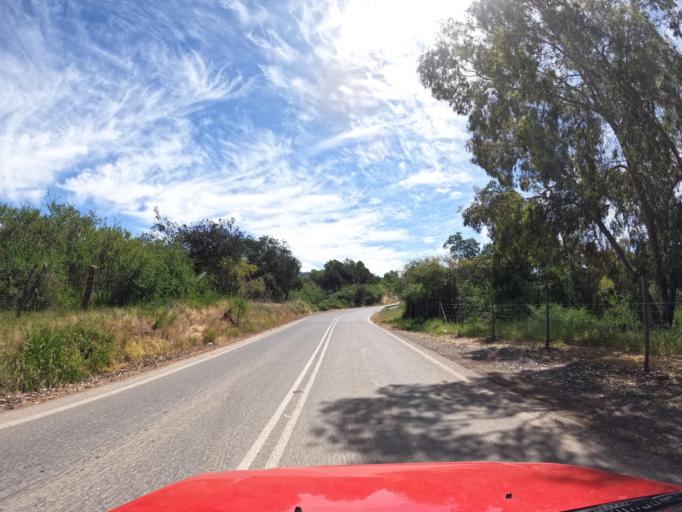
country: CL
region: Maule
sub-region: Provincia de Talca
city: Talca
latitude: -35.0025
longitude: -71.7979
